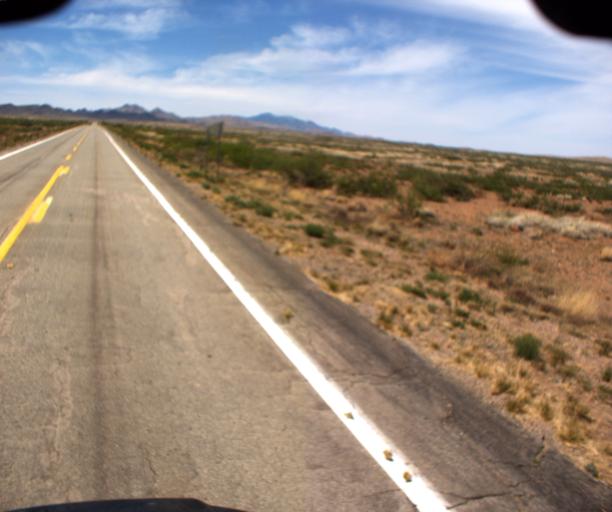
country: US
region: Arizona
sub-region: Cochise County
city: Willcox
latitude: 32.3764
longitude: -109.6435
